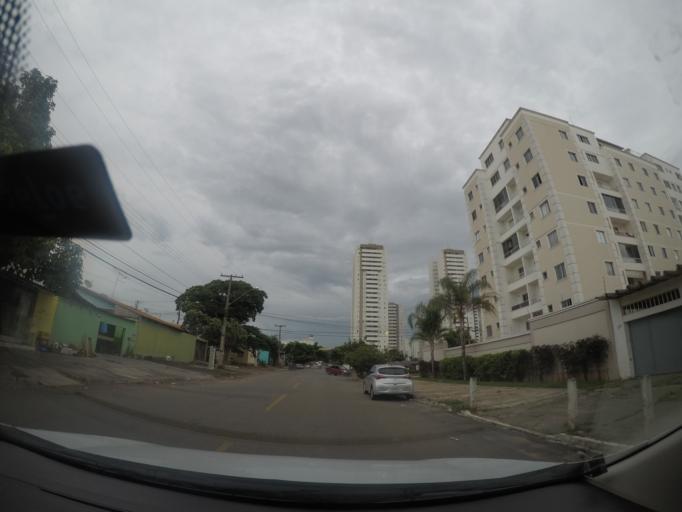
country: BR
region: Goias
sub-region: Goiania
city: Goiania
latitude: -16.6535
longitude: -49.2403
